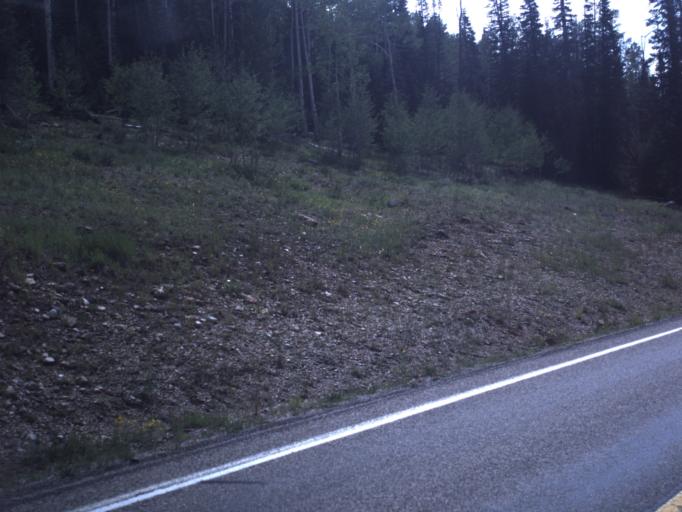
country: US
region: Utah
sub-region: Iron County
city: Cedar City
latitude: 37.5748
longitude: -112.8383
